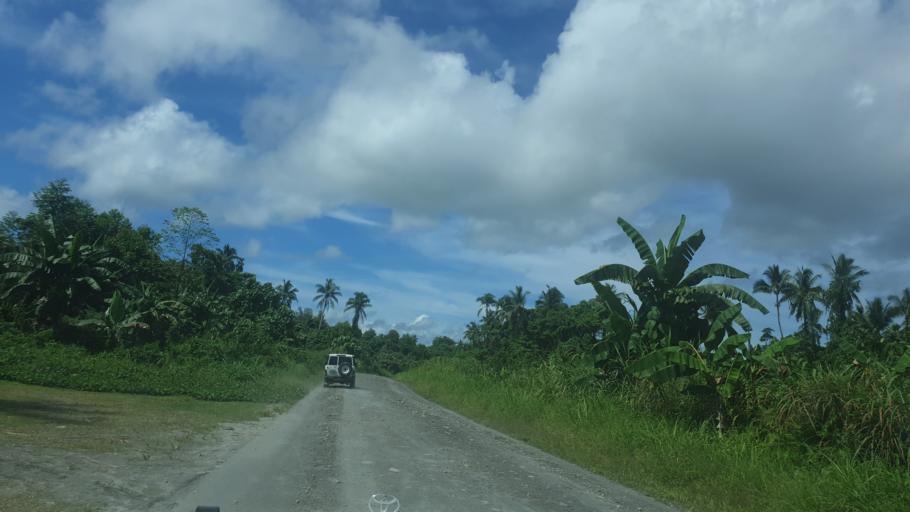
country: PG
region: Bougainville
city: Panguna
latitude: -6.5606
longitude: 155.3553
